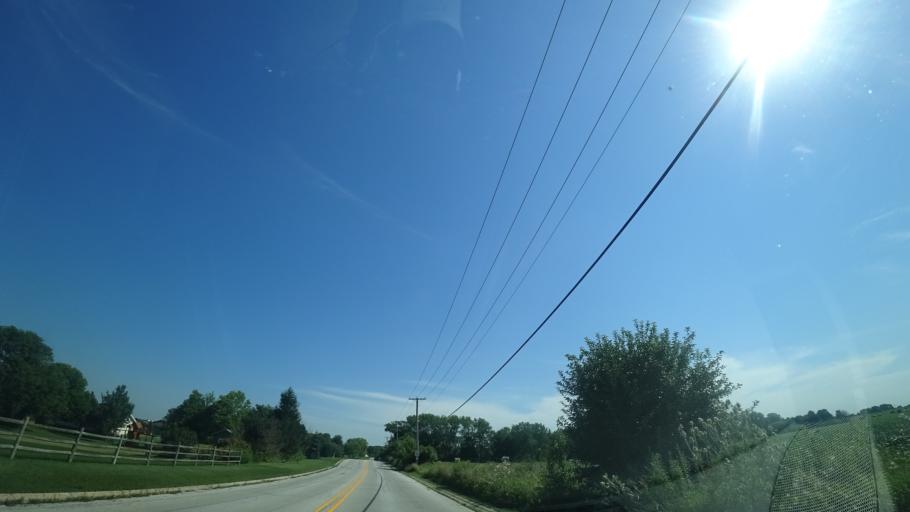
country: US
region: Illinois
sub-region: Will County
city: Homer Glen
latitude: 41.5681
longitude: -87.9096
